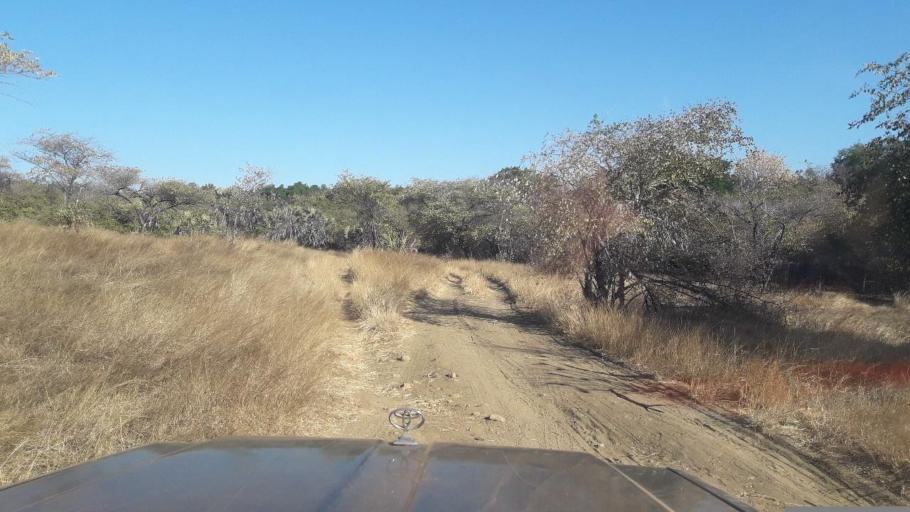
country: MG
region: Boeny
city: Sitampiky
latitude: -16.3933
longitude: 45.5933
